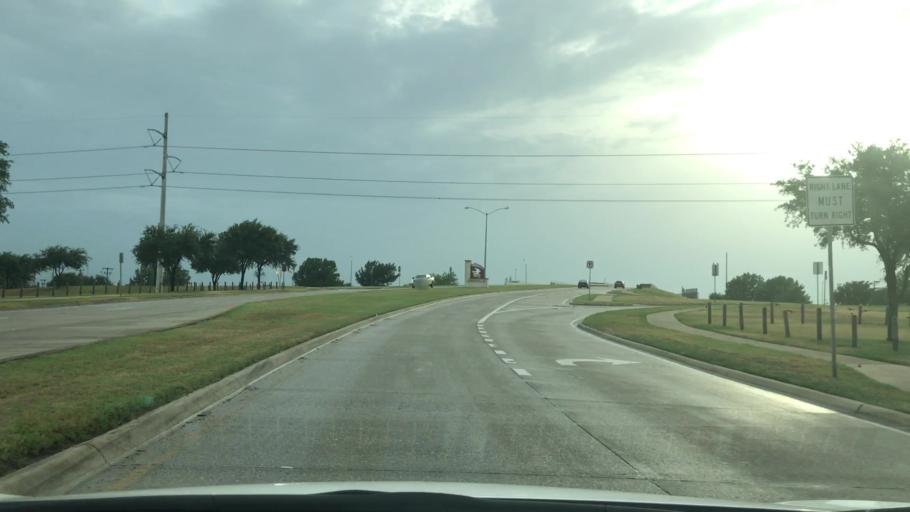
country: US
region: Texas
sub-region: Denton County
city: Lewisville
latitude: 33.0561
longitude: -97.0085
